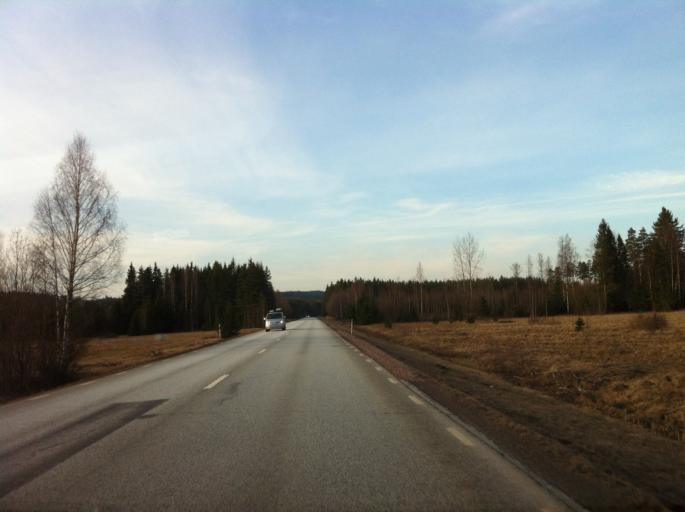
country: SE
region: Vaermland
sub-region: Storfors Kommun
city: Storfors
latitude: 59.5660
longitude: 14.2658
